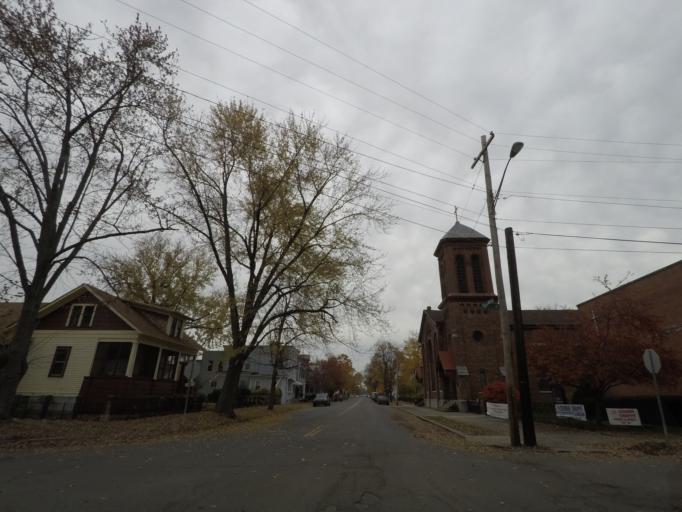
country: US
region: New York
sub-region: Saratoga County
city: Waterford
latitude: 42.7743
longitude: -73.6761
